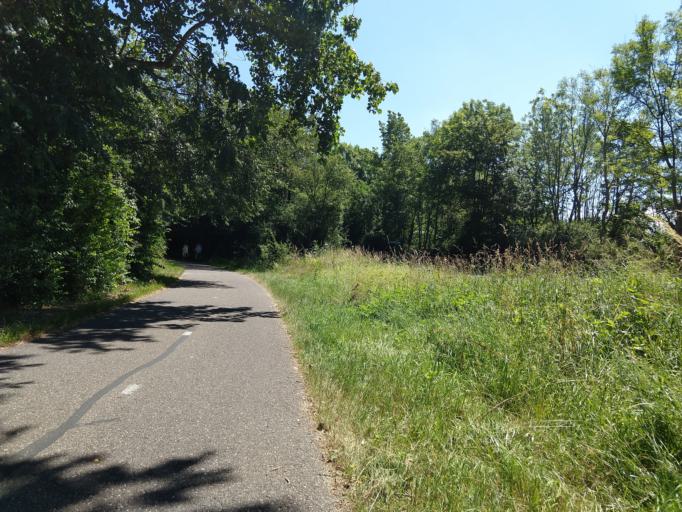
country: NL
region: Zeeland
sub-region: Gemeente Veere
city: Veere
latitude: 51.5556
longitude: 3.6537
